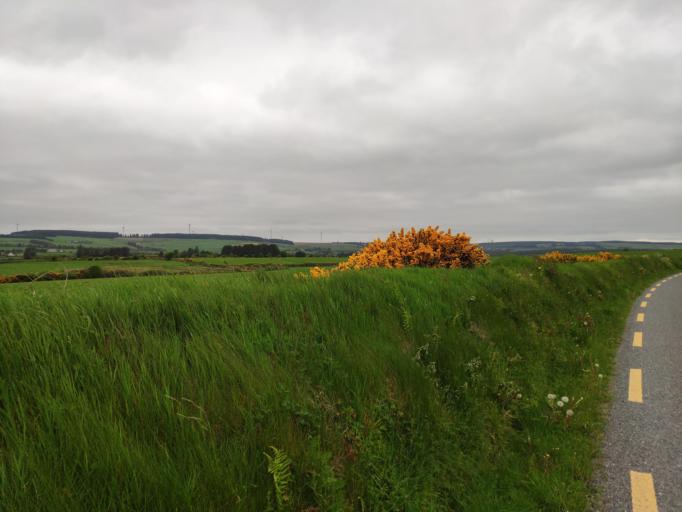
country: IE
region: Munster
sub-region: County Cork
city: Mallow
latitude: 52.0147
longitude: -8.7459
